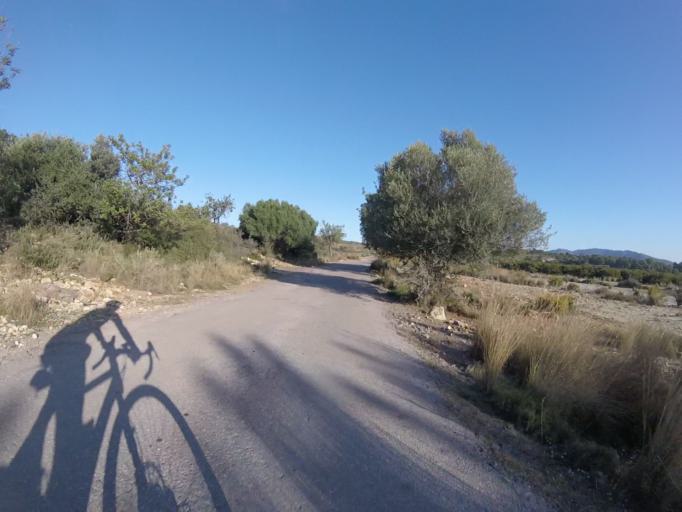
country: ES
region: Valencia
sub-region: Provincia de Castello
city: Torreblanca
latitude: 40.2280
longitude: 0.2007
